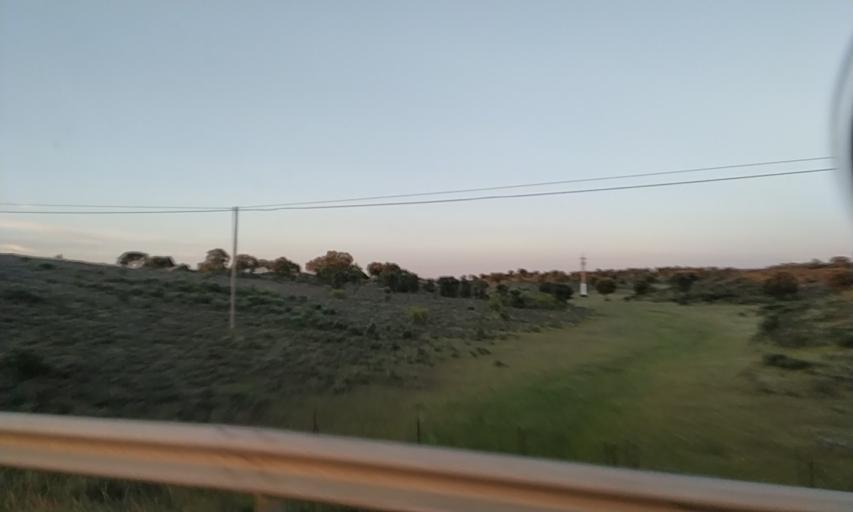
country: ES
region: Extremadura
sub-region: Provincia de Caceres
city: Alcantara
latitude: 39.6926
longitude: -6.8686
